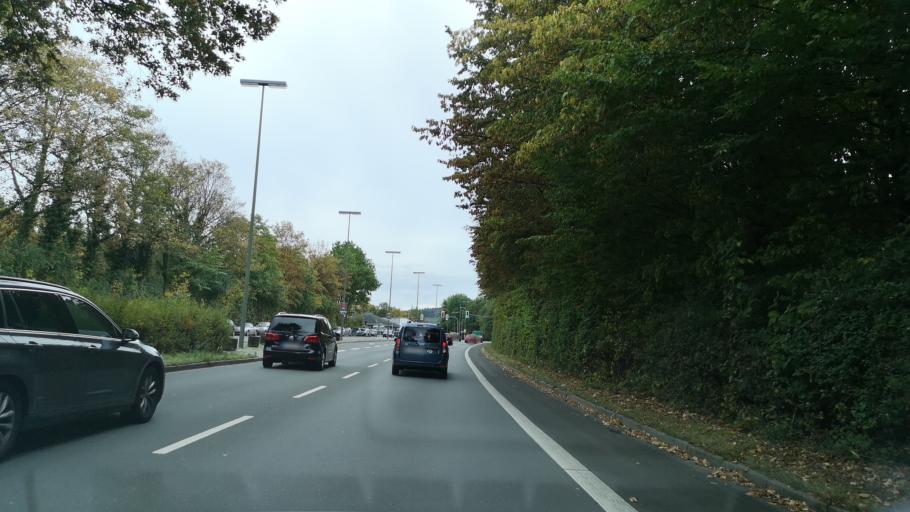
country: DE
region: North Rhine-Westphalia
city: Iserlohn
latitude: 51.3840
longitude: 7.7134
